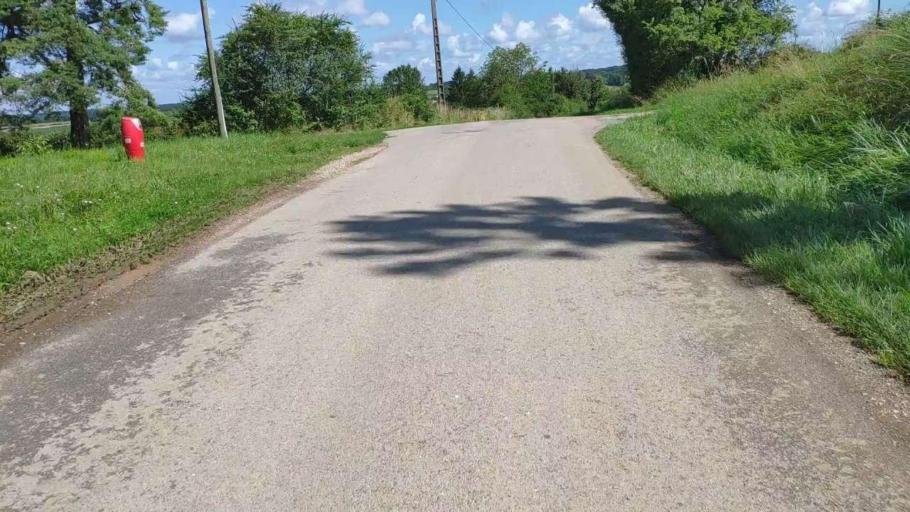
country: FR
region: Franche-Comte
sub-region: Departement du Jura
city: Bletterans
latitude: 46.8225
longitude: 5.5585
